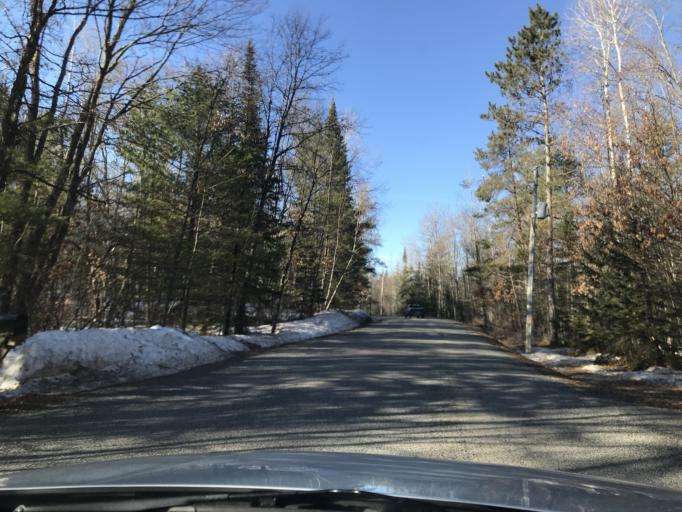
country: US
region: Wisconsin
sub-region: Marinette County
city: Niagara
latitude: 45.3913
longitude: -88.0577
